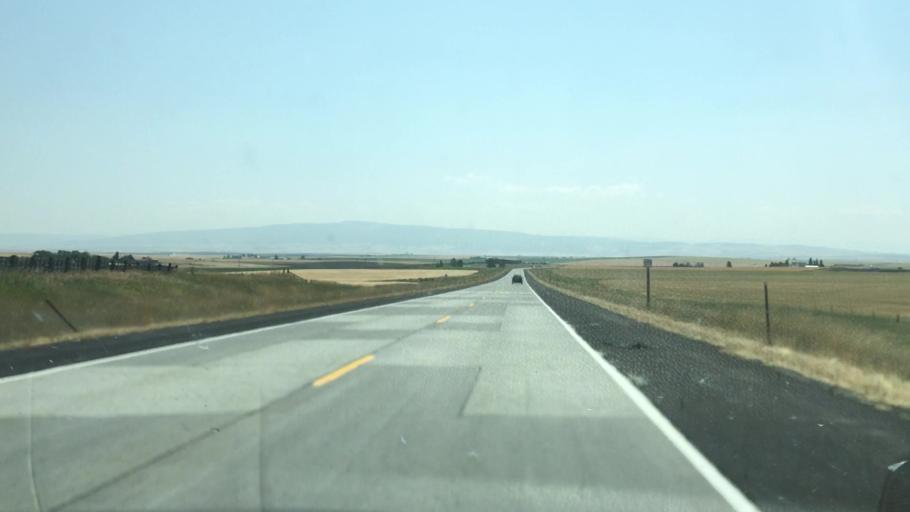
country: US
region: Idaho
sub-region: Lewis County
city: Nezperce
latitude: 46.0332
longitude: -116.3341
